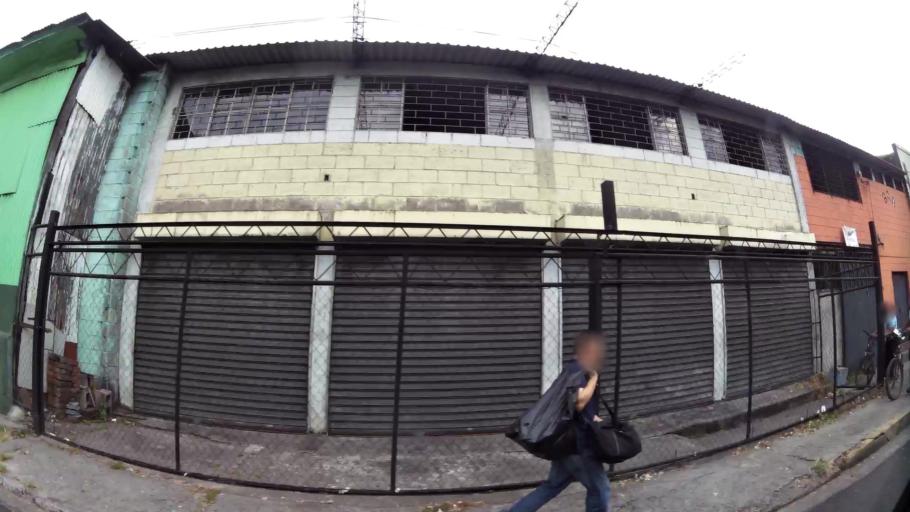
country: SV
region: San Salvador
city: San Salvador
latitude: 13.6977
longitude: -89.1869
